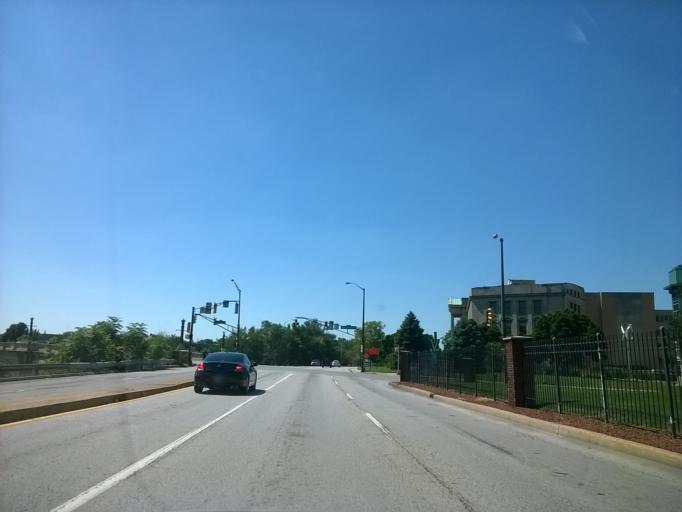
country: US
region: Indiana
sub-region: Marion County
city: Indianapolis
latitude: 39.8045
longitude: -86.1561
